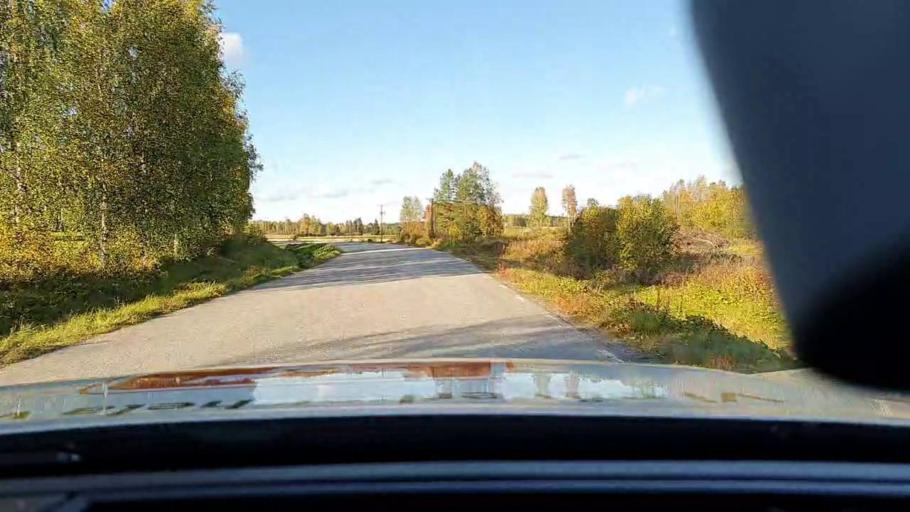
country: SE
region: Norrbotten
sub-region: Pitea Kommun
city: Norrfjarden
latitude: 65.5192
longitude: 21.4949
